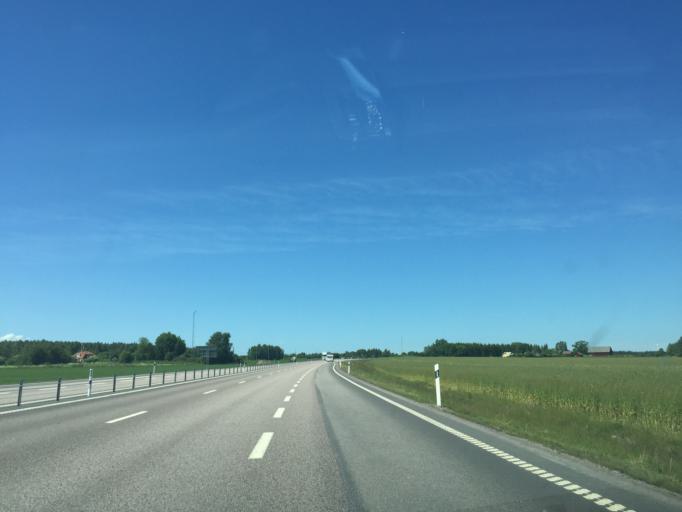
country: SE
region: OEstergoetland
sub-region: Motala Kommun
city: Stenstorp
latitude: 58.4048
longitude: 15.0875
